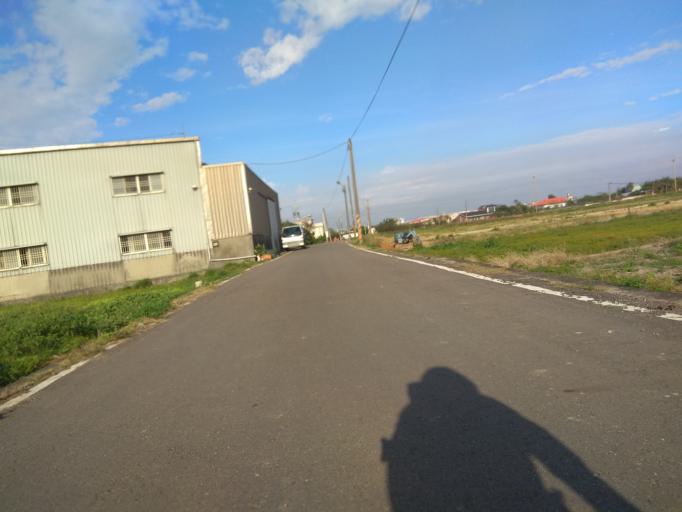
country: TW
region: Taiwan
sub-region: Hsinchu
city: Zhubei
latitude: 24.9775
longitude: 121.0583
